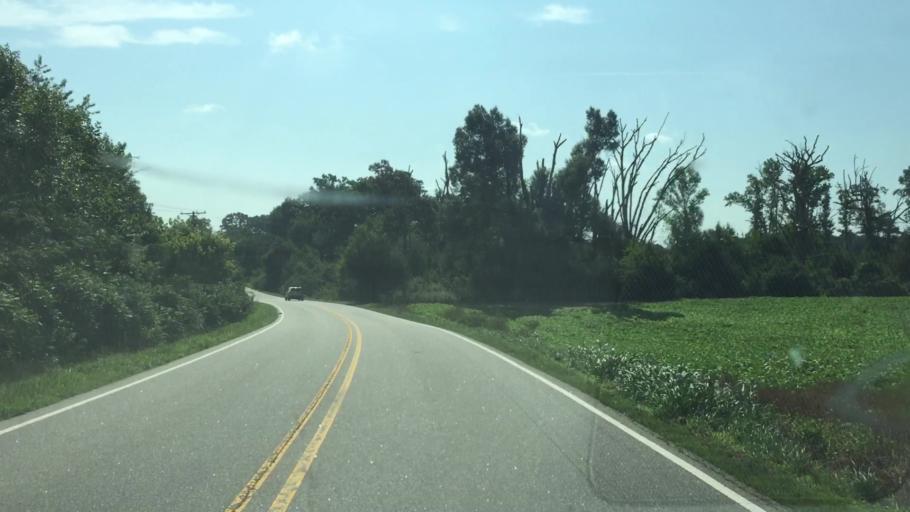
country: US
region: North Carolina
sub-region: Union County
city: Unionville
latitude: 35.1306
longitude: -80.4845
